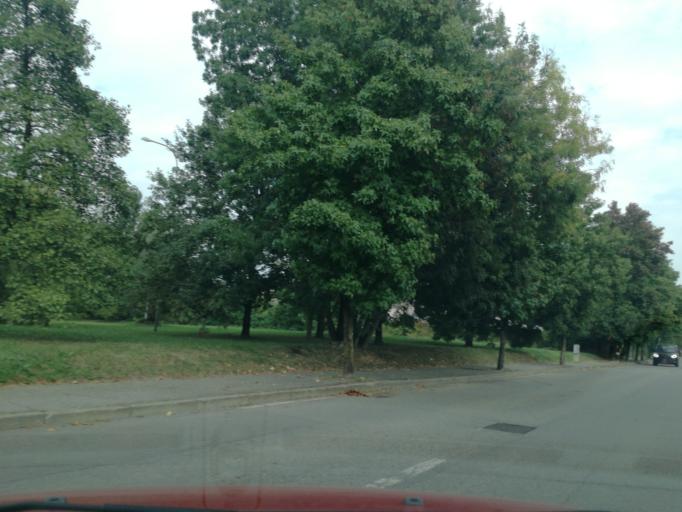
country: IT
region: Lombardy
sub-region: Provincia di Monza e Brianza
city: Carnate
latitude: 45.6428
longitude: 9.3794
